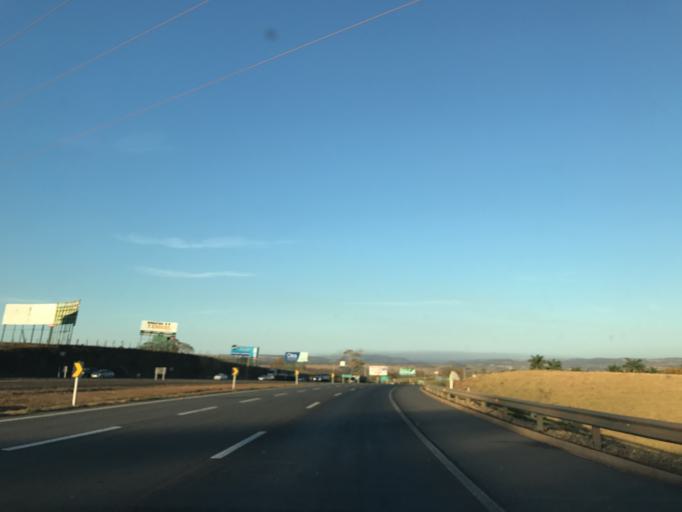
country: BR
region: Goias
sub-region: Goianapolis
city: Goianapolis
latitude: -16.4462
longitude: -49.0209
